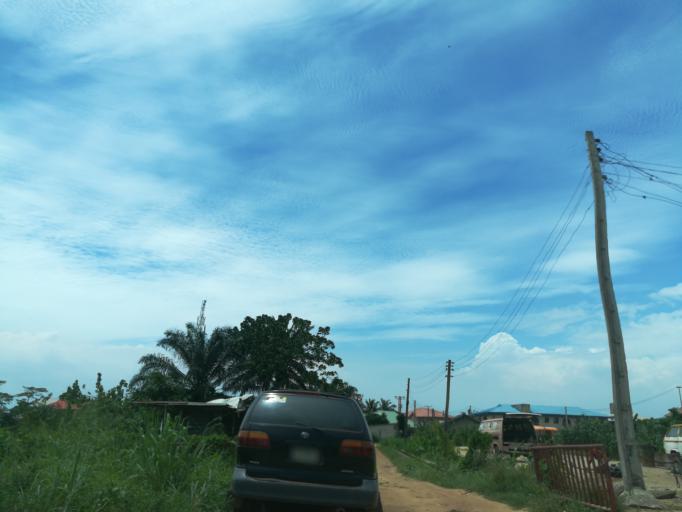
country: NG
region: Lagos
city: Ebute Ikorodu
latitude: 6.5847
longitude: 3.4918
